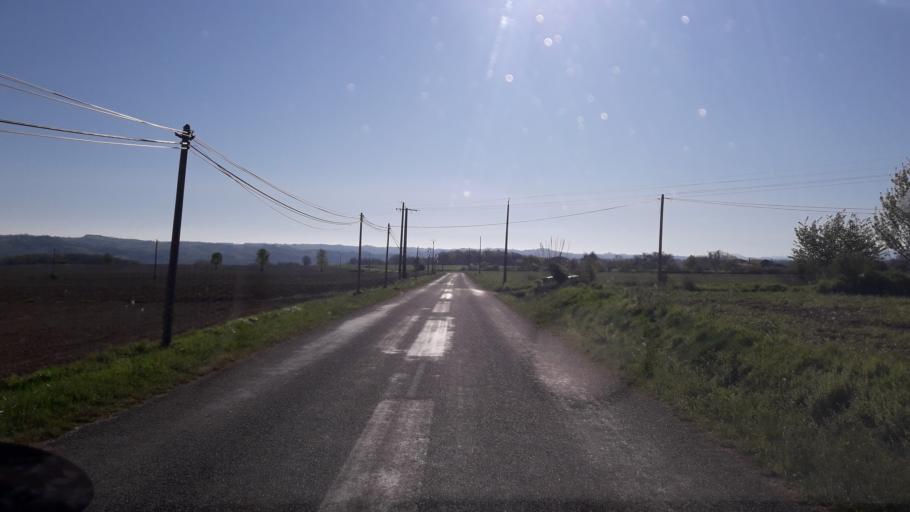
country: FR
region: Midi-Pyrenees
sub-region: Departement de la Haute-Garonne
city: Montesquieu-Volvestre
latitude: 43.2002
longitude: 1.1889
